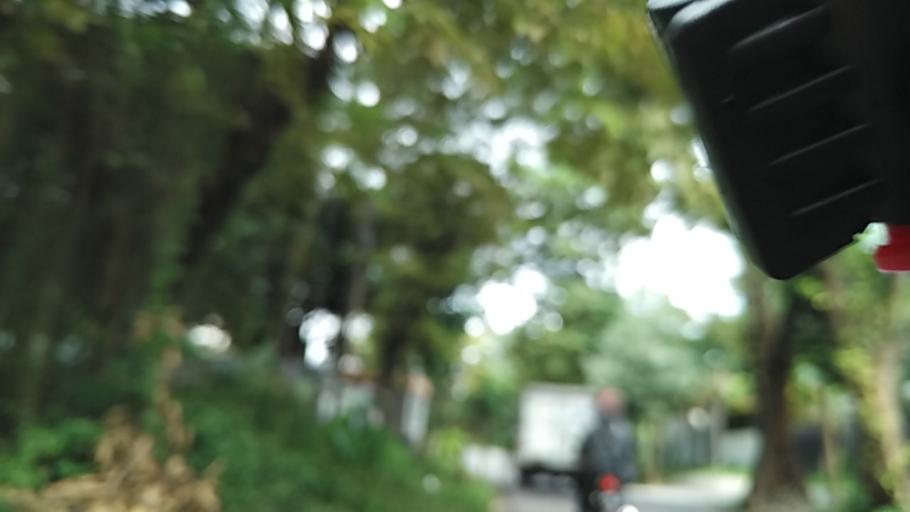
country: ID
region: Central Java
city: Semarang
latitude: -7.0042
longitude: 110.4119
